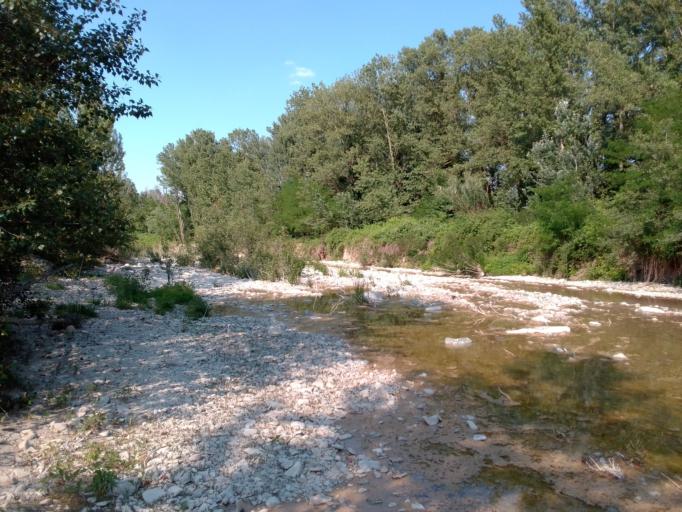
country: IT
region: Emilia-Romagna
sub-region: Provincia di Piacenza
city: Borgonovo Valtidone
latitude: 44.9765
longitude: 9.4594
